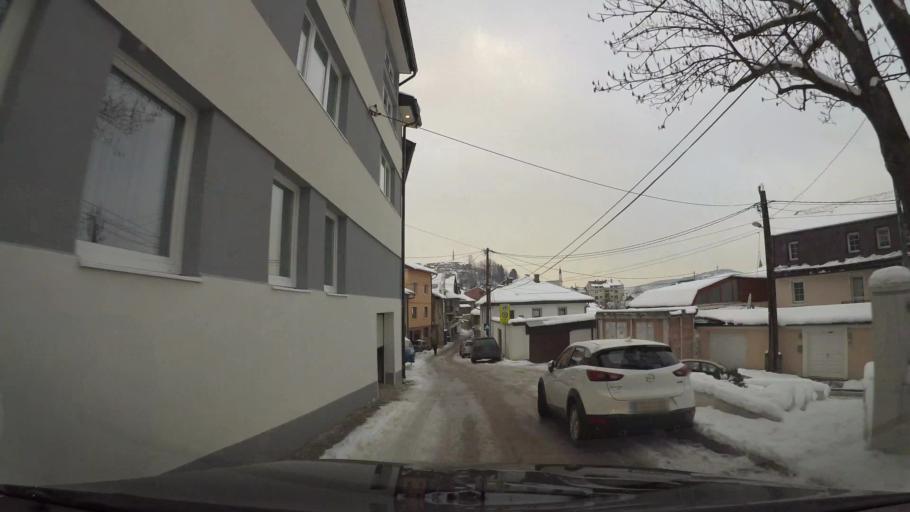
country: BA
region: Federation of Bosnia and Herzegovina
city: Kobilja Glava
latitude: 43.8548
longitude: 18.4342
